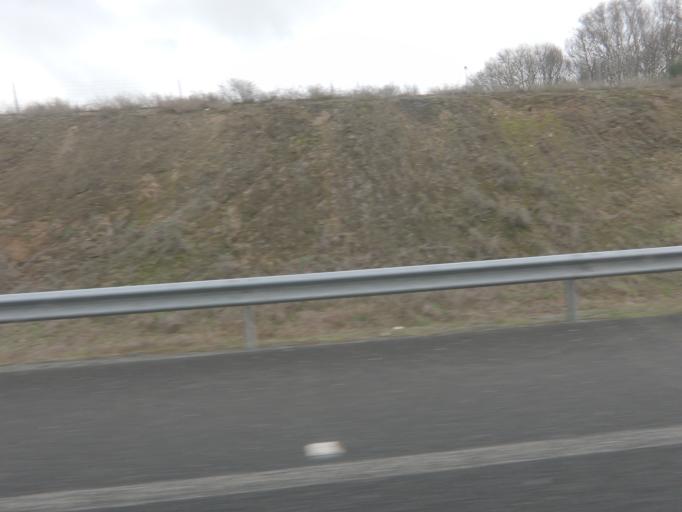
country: ES
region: Galicia
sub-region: Provincia de Pontevedra
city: Lalin
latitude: 42.6434
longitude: -8.1324
